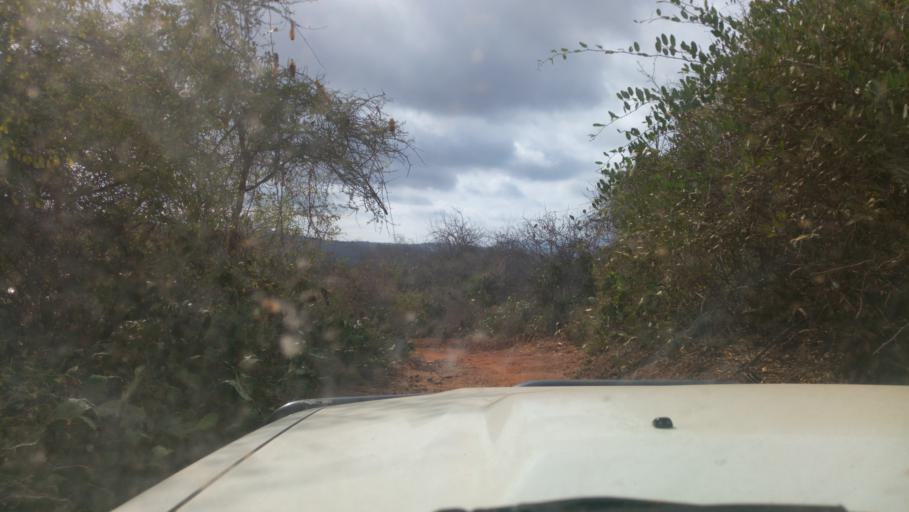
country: KE
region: Kitui
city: Kitui
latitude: -1.8559
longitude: 38.2543
